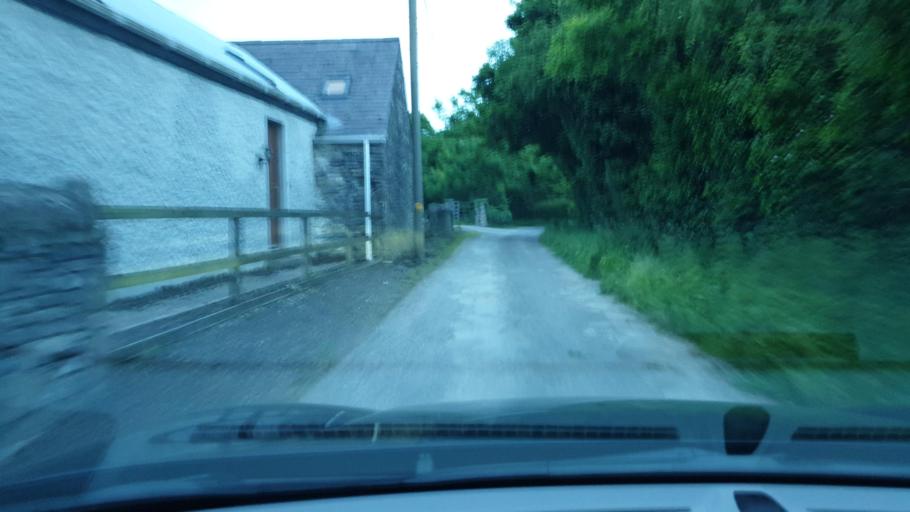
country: IE
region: Leinster
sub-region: An Mhi
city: Duleek
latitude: 53.5927
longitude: -6.3654
